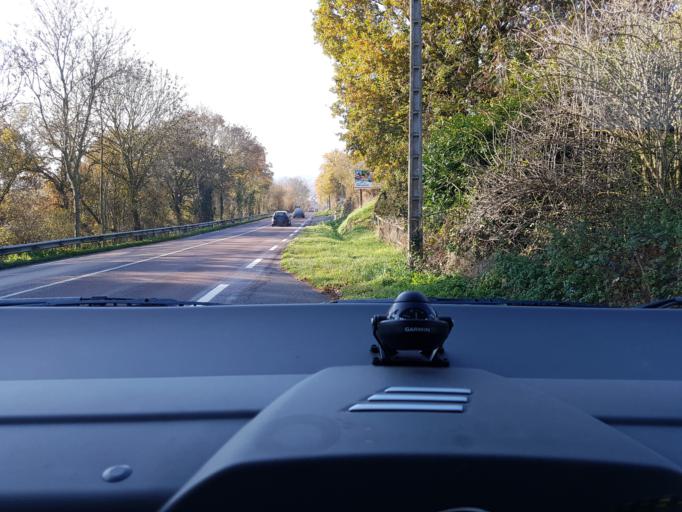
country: FR
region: Lower Normandy
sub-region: Departement du Calvados
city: Thury-Harcourt
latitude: 48.9904
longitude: -0.4687
